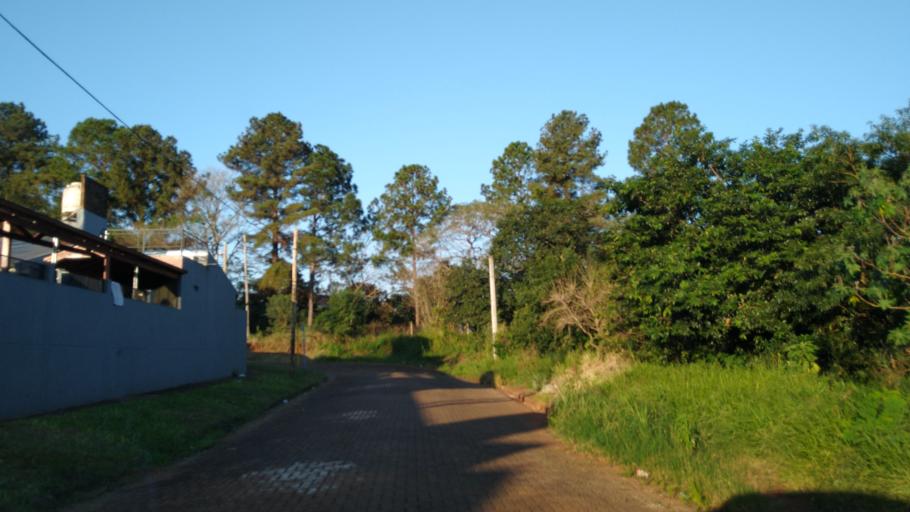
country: AR
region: Misiones
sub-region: Departamento de Capital
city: Posadas
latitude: -27.4311
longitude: -55.9236
